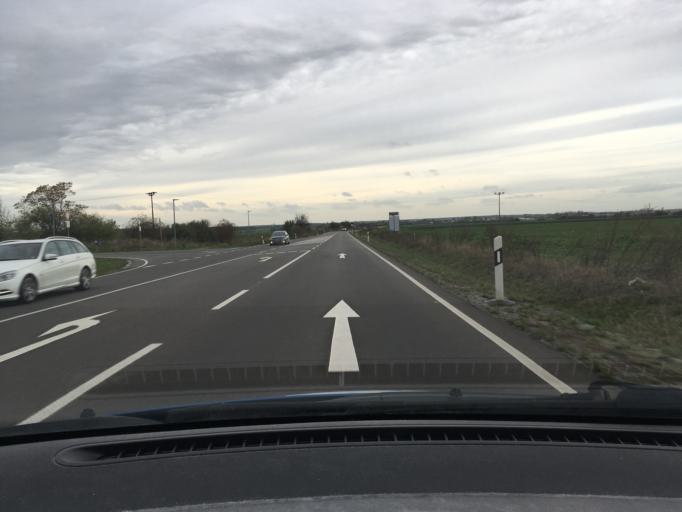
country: DE
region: Saxony-Anhalt
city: Leitzkau
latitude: 52.0629
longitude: 11.9074
